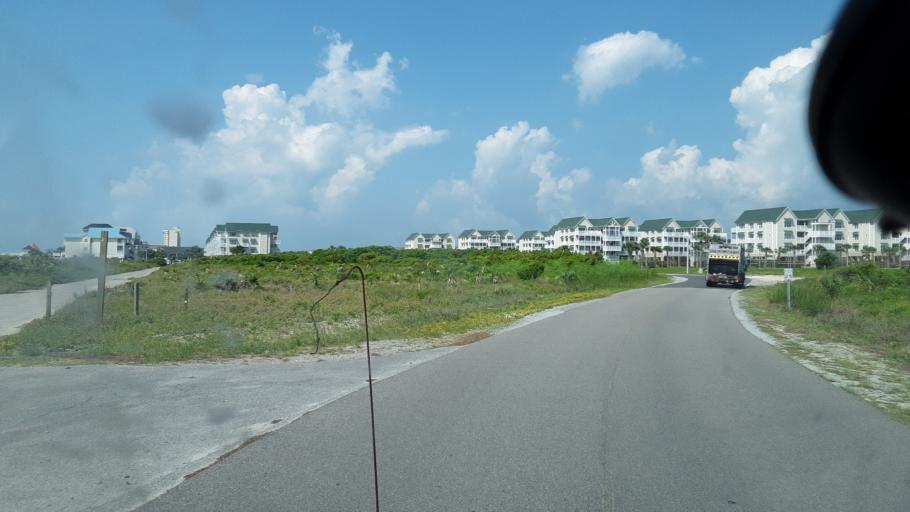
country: US
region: North Carolina
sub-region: Brunswick County
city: Sunset Beach
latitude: 33.8818
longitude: -78.4587
